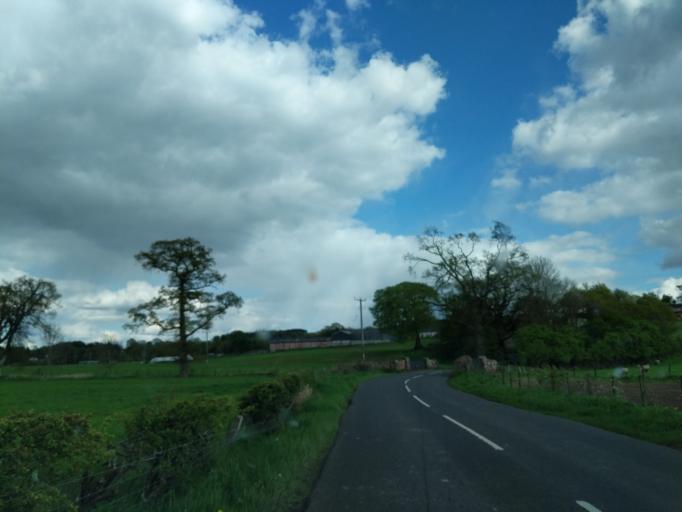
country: GB
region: Scotland
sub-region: Stirling
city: Balfron
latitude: 56.1288
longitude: -4.2395
